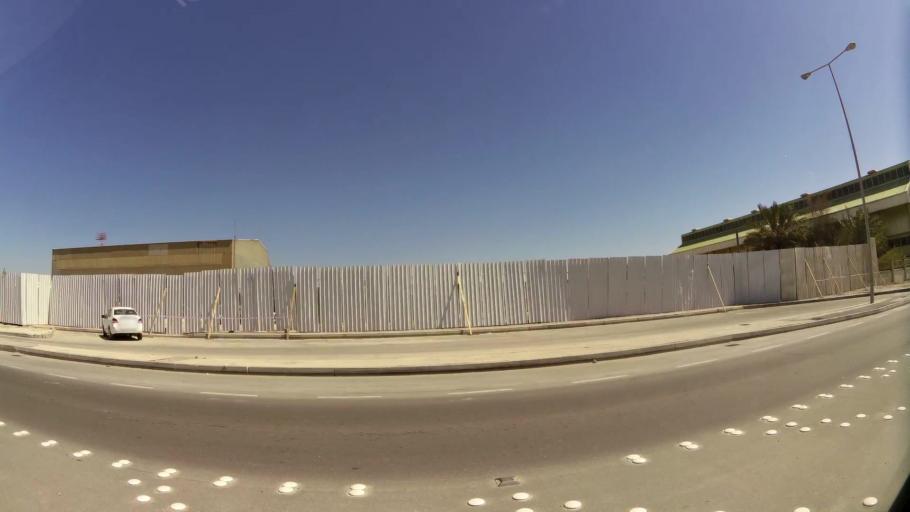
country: BH
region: Muharraq
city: Al Muharraq
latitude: 26.2730
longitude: 50.6140
